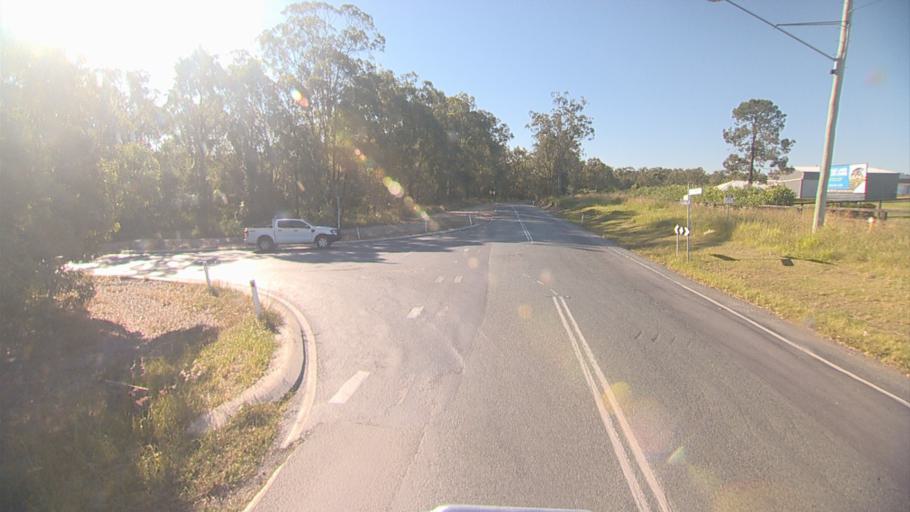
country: AU
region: Queensland
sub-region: Logan
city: Logan Reserve
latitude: -27.7510
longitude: 153.1312
